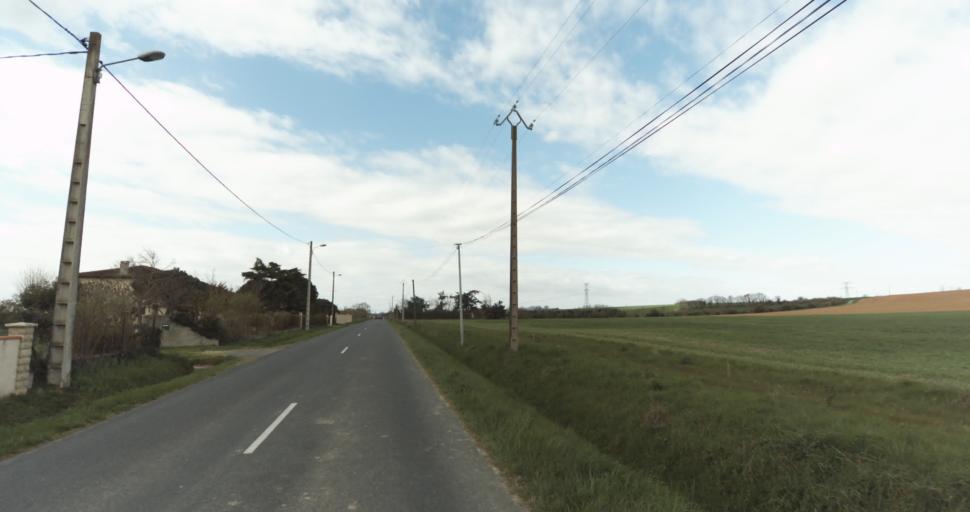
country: FR
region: Midi-Pyrenees
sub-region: Departement de la Haute-Garonne
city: Auterive
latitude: 43.3790
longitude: 1.4623
